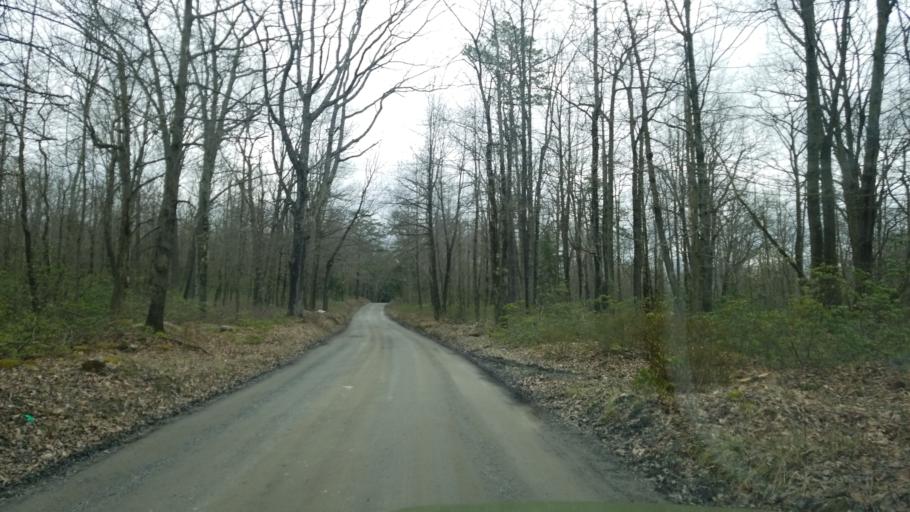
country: US
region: Pennsylvania
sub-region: Clearfield County
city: Shiloh
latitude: 41.1700
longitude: -78.2819
